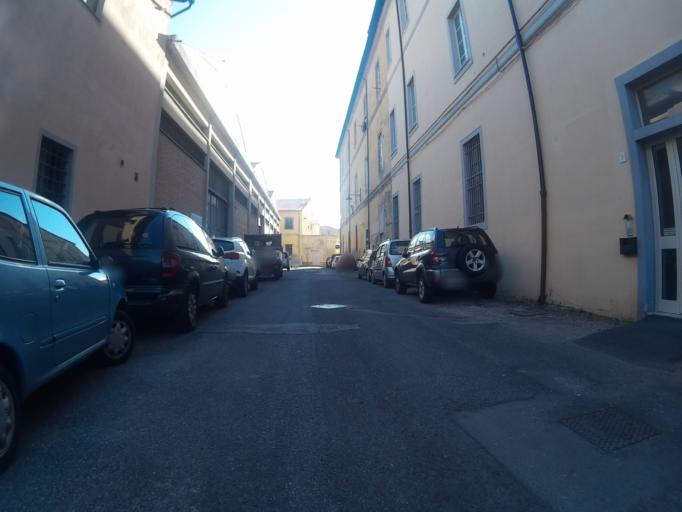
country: IT
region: Tuscany
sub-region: Provincia di Livorno
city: Livorno
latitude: 43.5591
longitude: 10.3117
